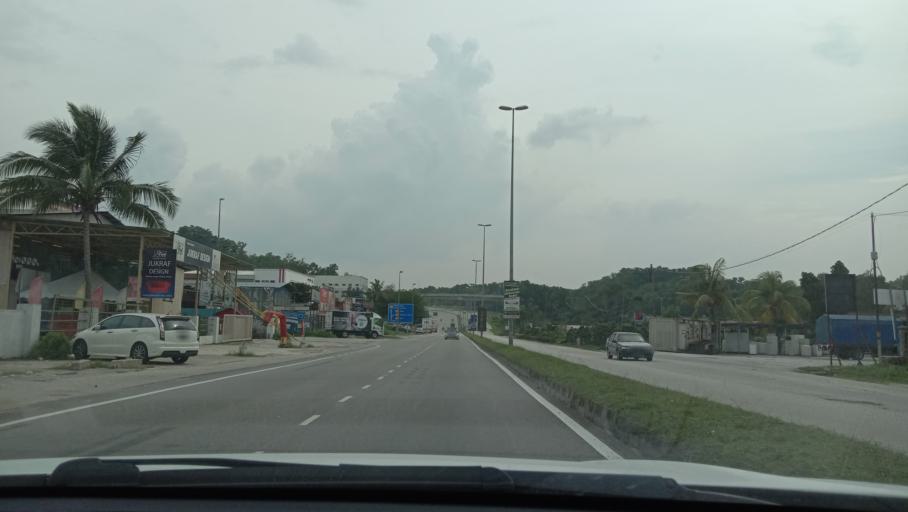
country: MY
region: Selangor
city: Kampung Baru Subang
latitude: 3.1331
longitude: 101.5259
